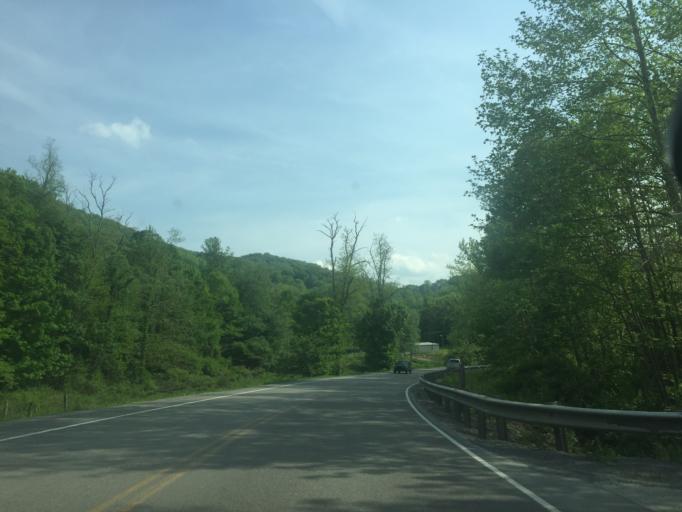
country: US
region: West Virginia
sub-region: Tucker County
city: Parsons
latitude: 38.9542
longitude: -79.5000
